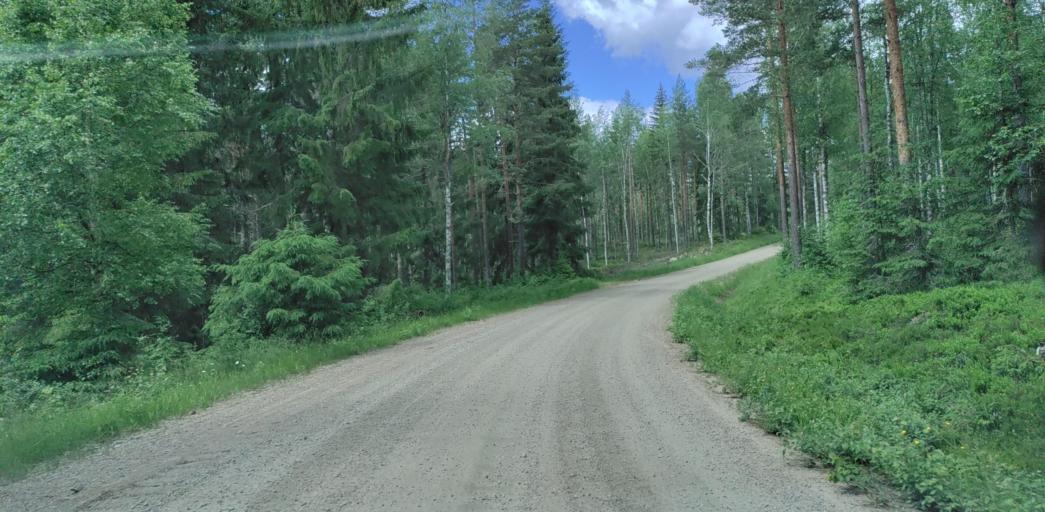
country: SE
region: Vaermland
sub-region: Hagfors Kommun
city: Ekshaerad
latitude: 60.0934
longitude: 13.4046
